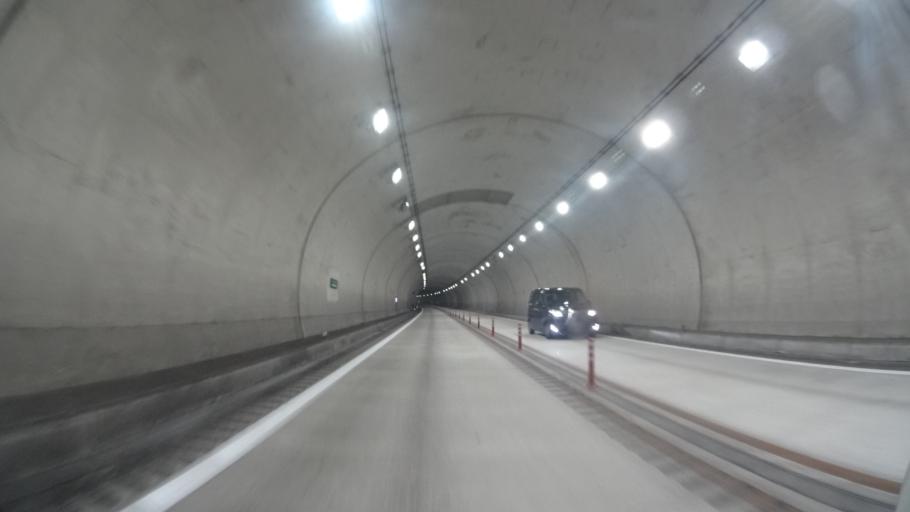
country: JP
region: Shimane
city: Odacho-oda
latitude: 35.1383
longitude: 132.4079
